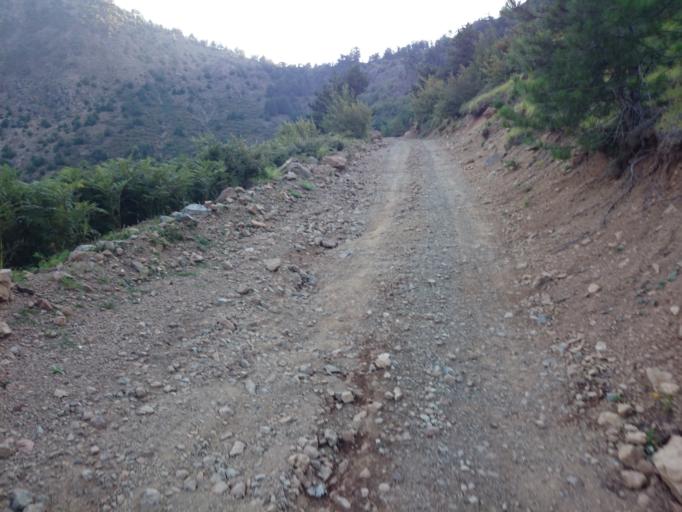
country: AL
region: Lezhe
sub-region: Rrethi i Mirdites
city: Orosh
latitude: 41.8672
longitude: 20.0910
